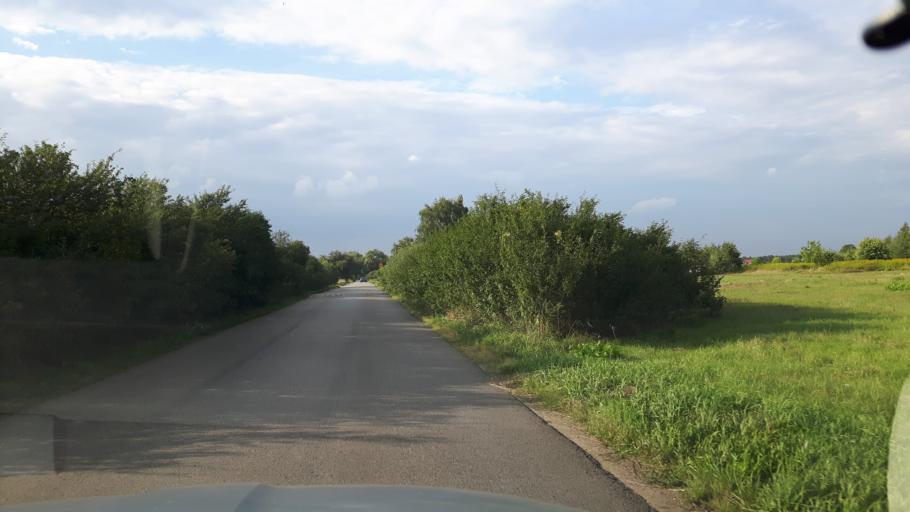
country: PL
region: Masovian Voivodeship
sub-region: Powiat wolominski
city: Marki
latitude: 52.3310
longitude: 21.0748
